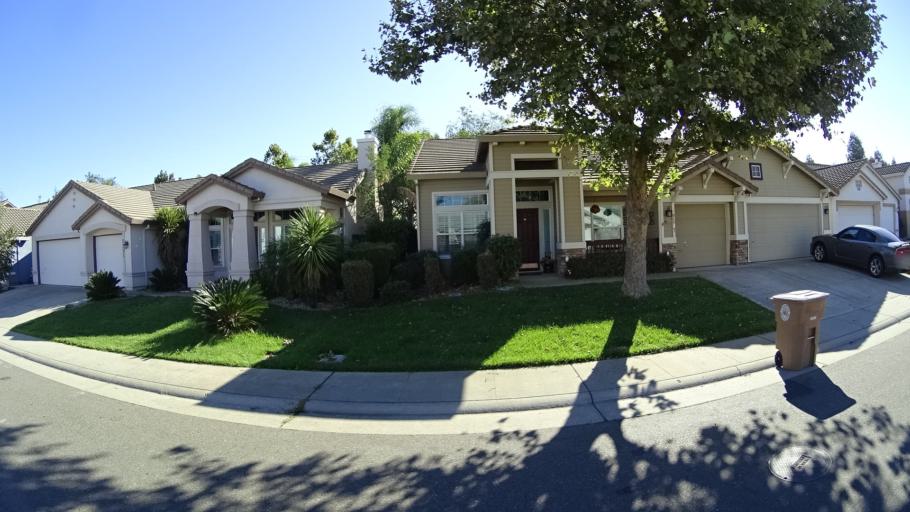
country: US
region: California
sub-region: Sacramento County
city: Vineyard
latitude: 38.4484
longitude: -121.3540
